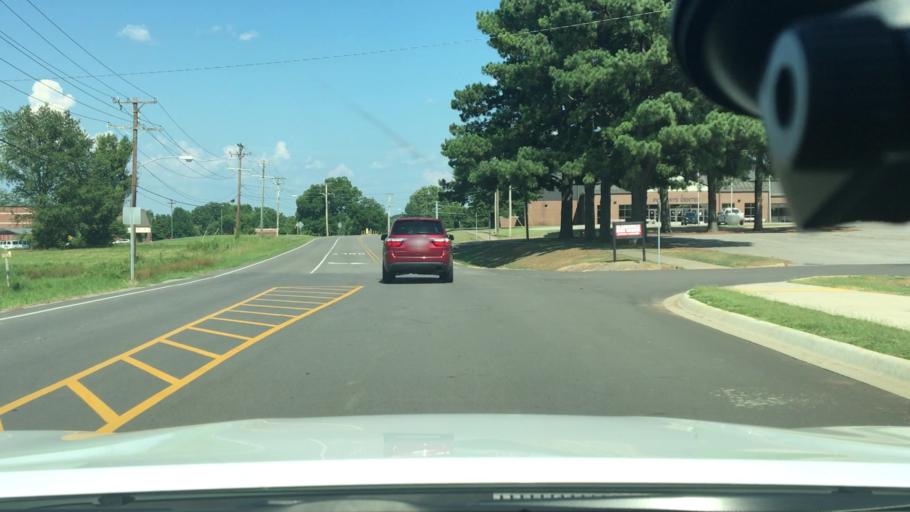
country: US
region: Arkansas
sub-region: Johnson County
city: Clarksville
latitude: 35.4617
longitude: -93.4845
